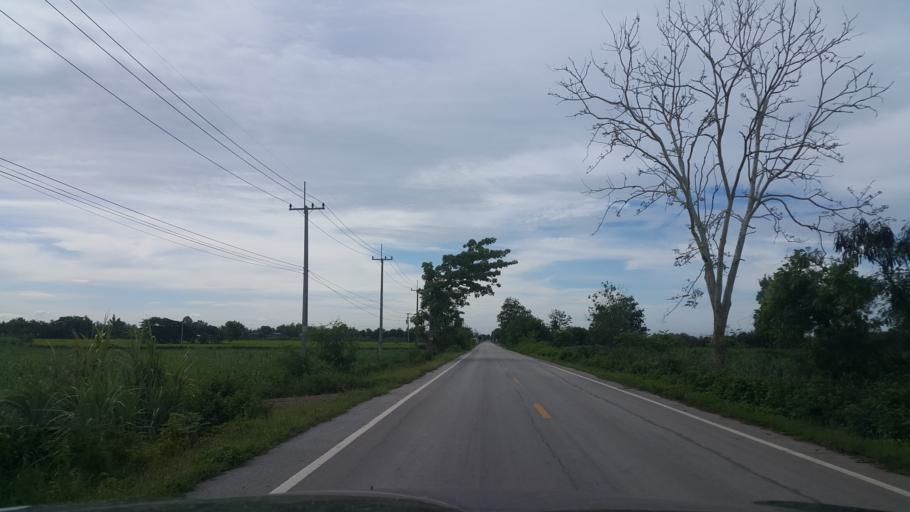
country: TH
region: Sukhothai
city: Si Nakhon
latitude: 17.2760
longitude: 99.9784
